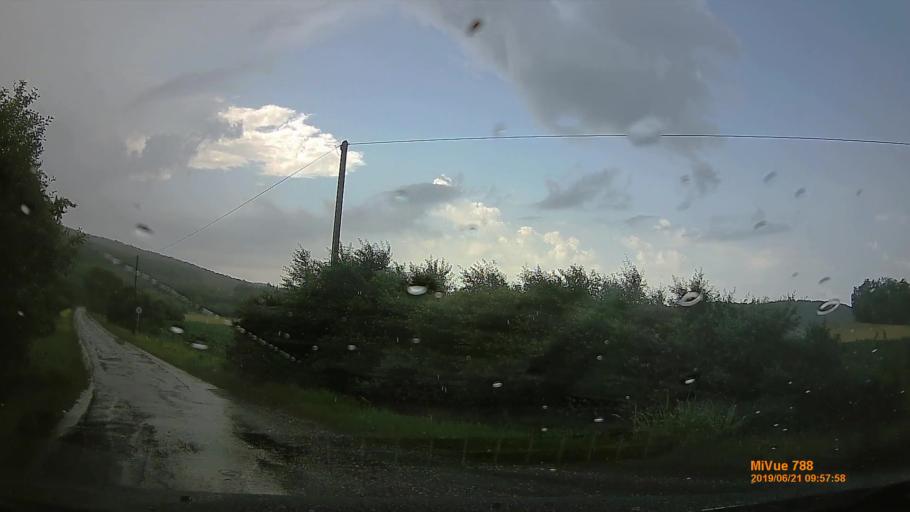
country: HU
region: Baranya
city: Buekkoesd
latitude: 46.2179
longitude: 17.9704
